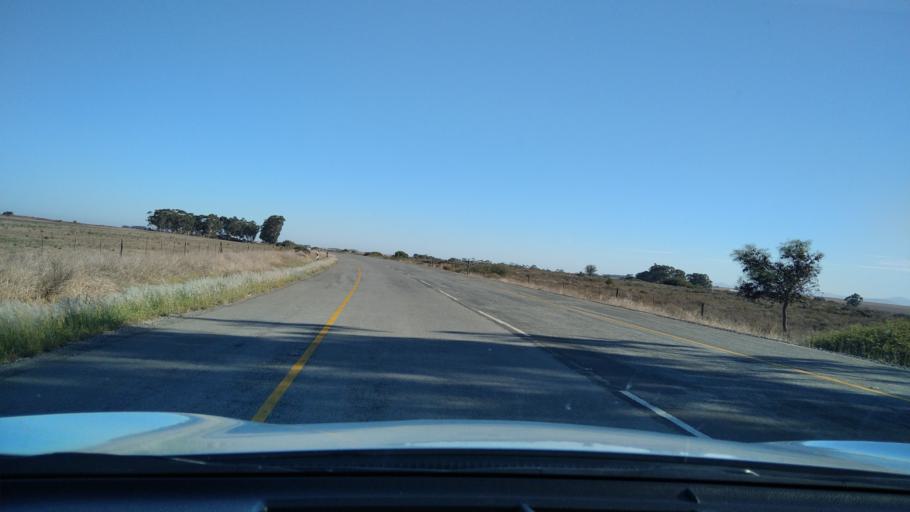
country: ZA
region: Western Cape
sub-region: West Coast District Municipality
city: Moorreesburg
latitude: -33.2681
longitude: 18.5985
